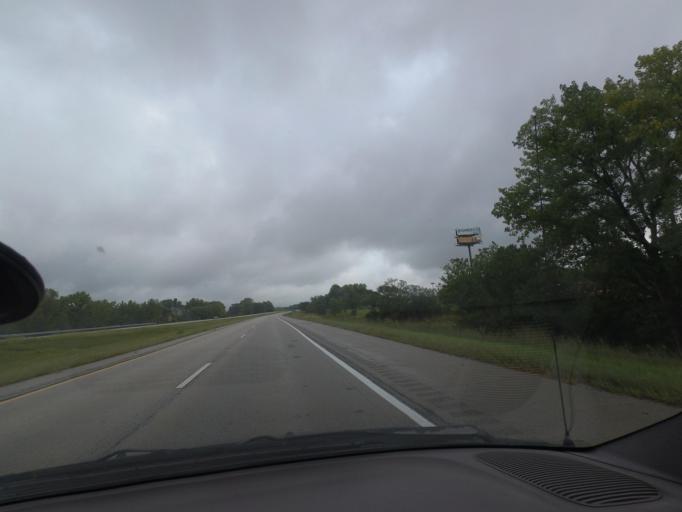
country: US
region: Illinois
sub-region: Piatt County
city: Monticello
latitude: 40.0499
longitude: -88.5730
